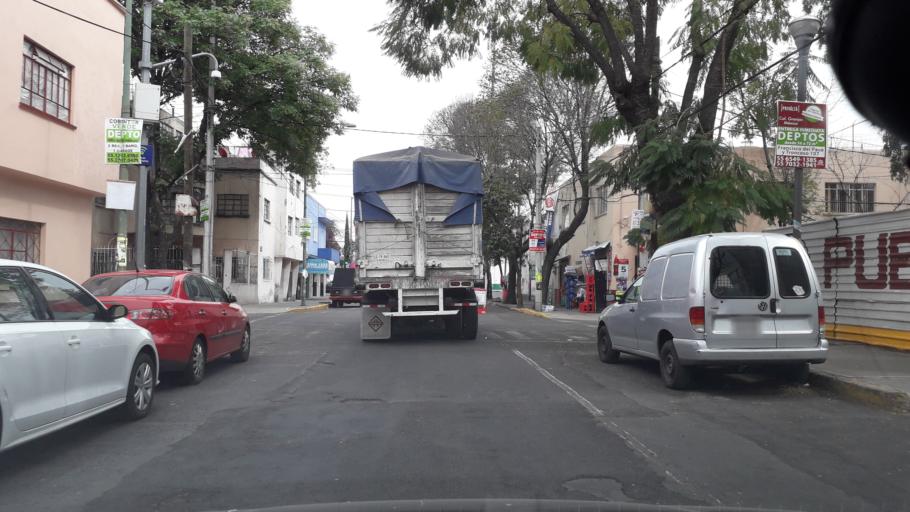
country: MX
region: Mexico City
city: Mexico City
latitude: 19.4099
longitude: -99.1322
